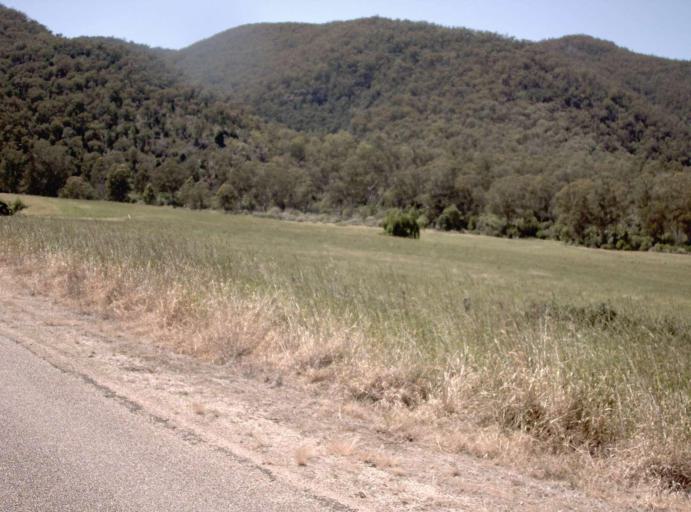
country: AU
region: Victoria
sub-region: East Gippsland
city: Lakes Entrance
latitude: -37.3966
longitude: 148.2149
